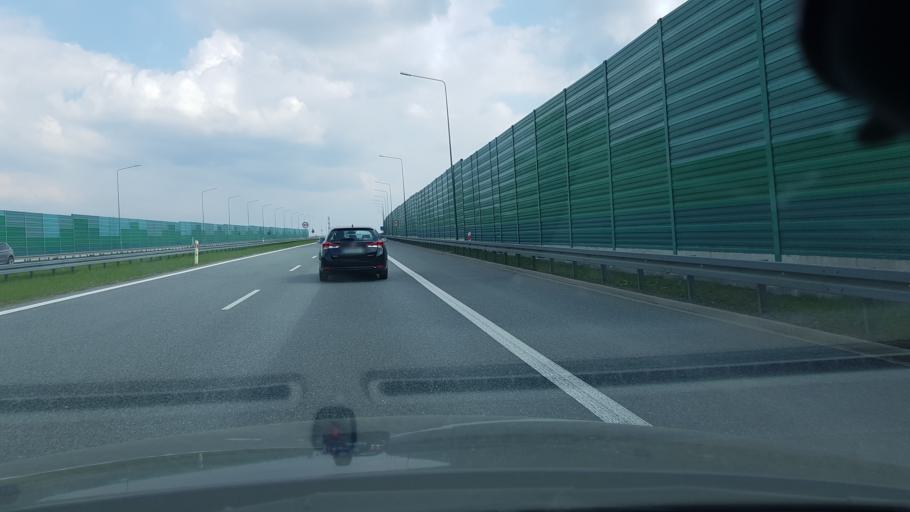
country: PL
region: Masovian Voivodeship
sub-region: Powiat minski
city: Kaluszyn
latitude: 52.2004
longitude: 21.7640
